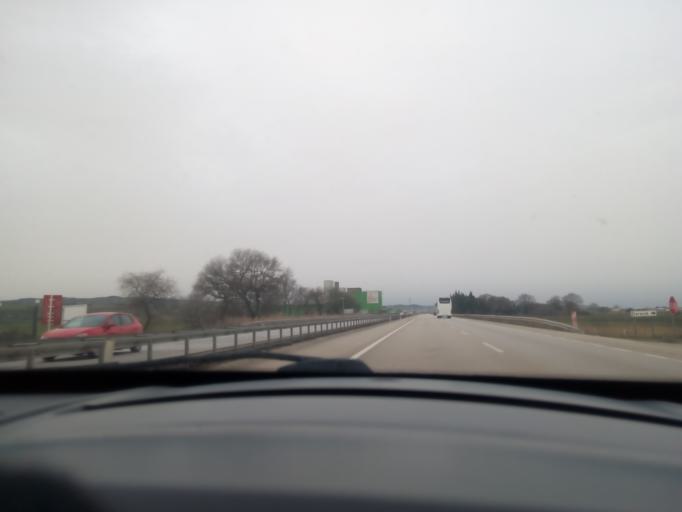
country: TR
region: Bursa
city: Tatkavakli
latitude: 40.0304
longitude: 28.3300
